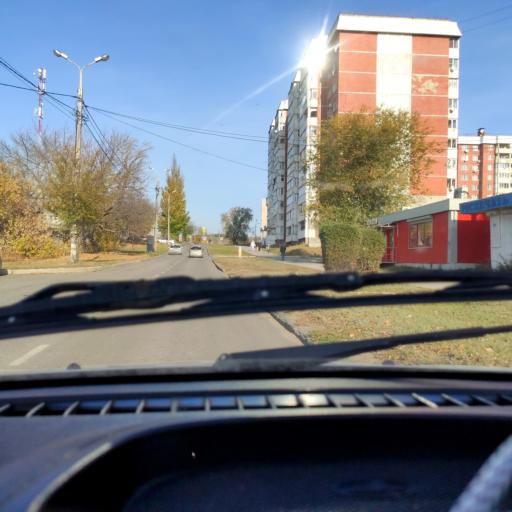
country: RU
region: Samara
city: Zhigulevsk
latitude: 53.4699
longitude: 49.5308
